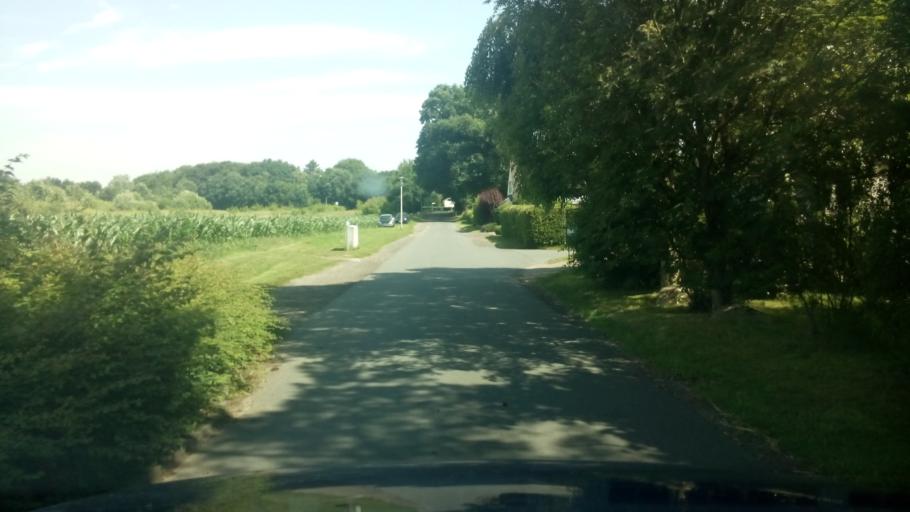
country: DE
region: Lower Saxony
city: Osterholz-Scharmbeck
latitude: 53.2503
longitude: 8.8190
